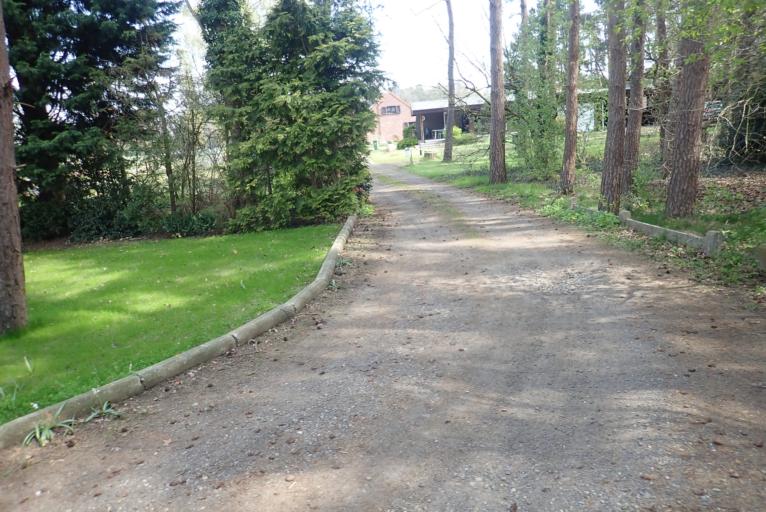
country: BE
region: Flanders
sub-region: Provincie Antwerpen
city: Zoersel
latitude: 51.2272
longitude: 4.7029
